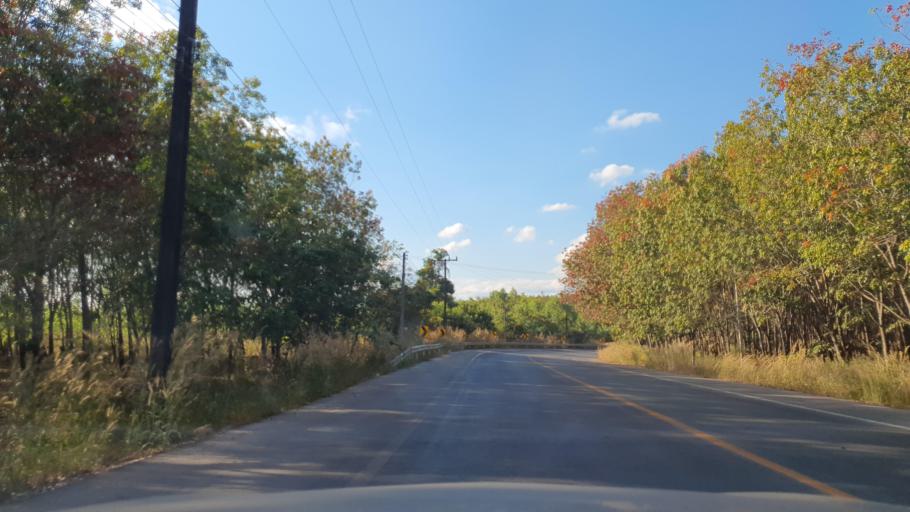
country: TH
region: Nong Khai
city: Bueng Khong Long
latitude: 18.0138
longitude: 104.0027
